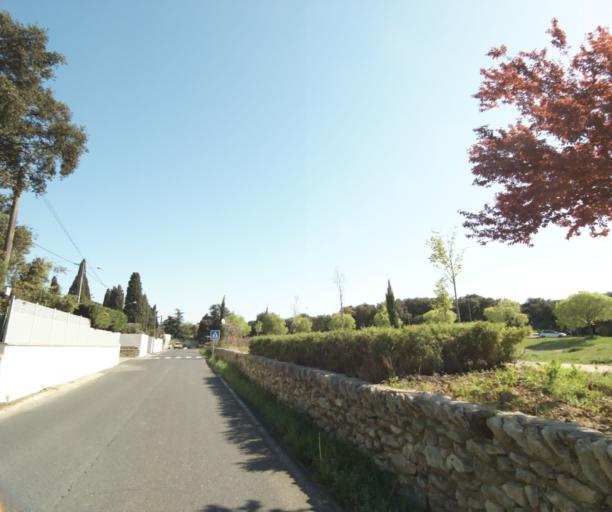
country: FR
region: Languedoc-Roussillon
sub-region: Departement de l'Herault
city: Castries
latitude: 43.6815
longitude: 3.9847
